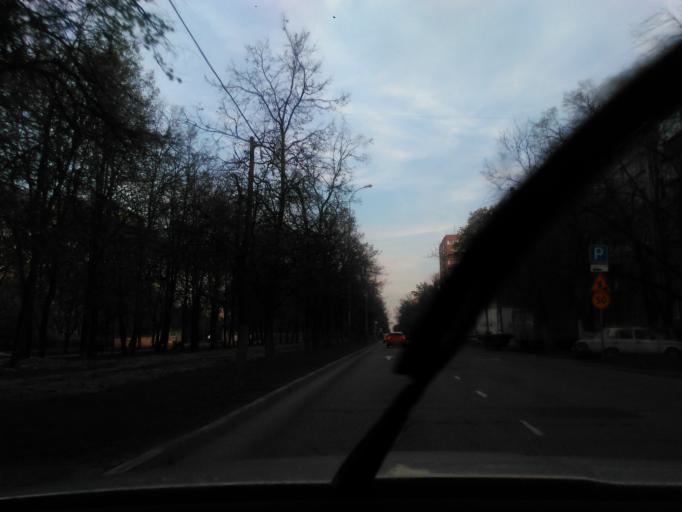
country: RU
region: Moscow
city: Novyye Kuz'minki
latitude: 55.7057
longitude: 37.7468
